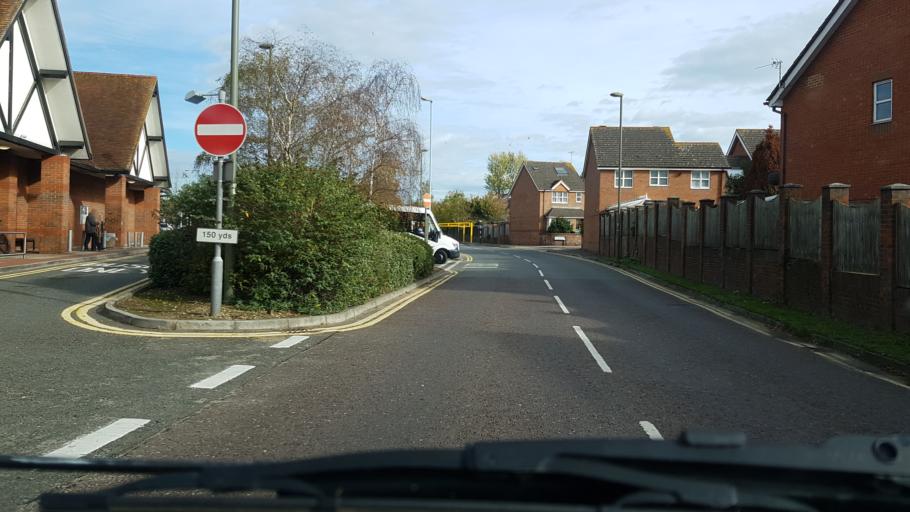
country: GB
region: England
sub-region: Surrey
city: Cobham
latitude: 51.3359
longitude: -0.4214
